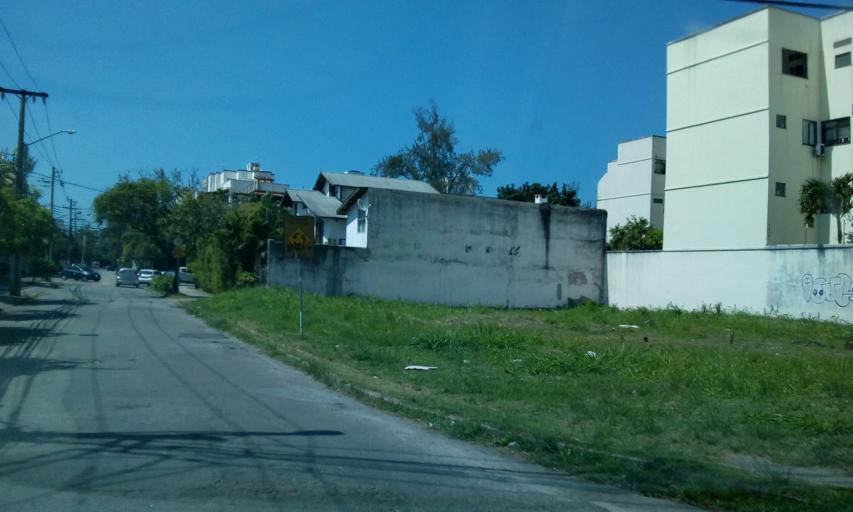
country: BR
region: Rio de Janeiro
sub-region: Nilopolis
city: Nilopolis
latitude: -23.0195
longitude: -43.4737
